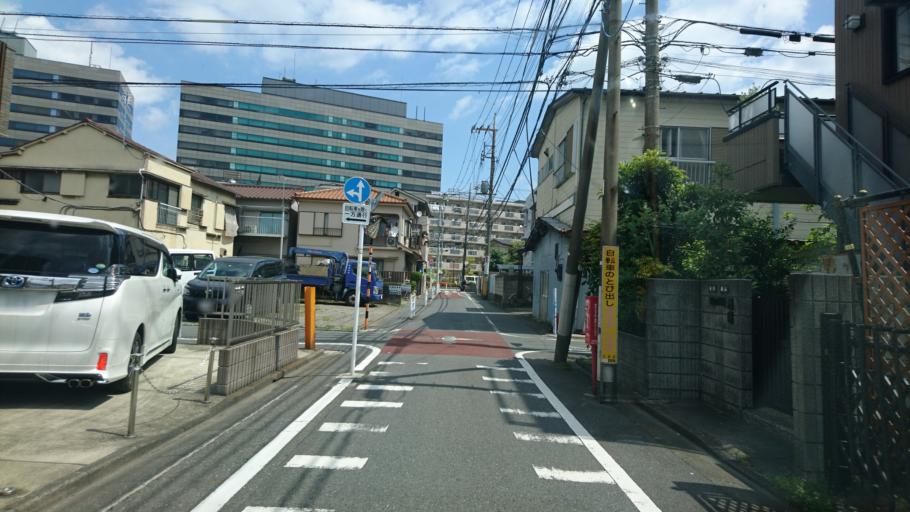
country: JP
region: Kanagawa
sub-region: Kawasaki-shi
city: Kawasaki
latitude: 35.5540
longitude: 139.7215
